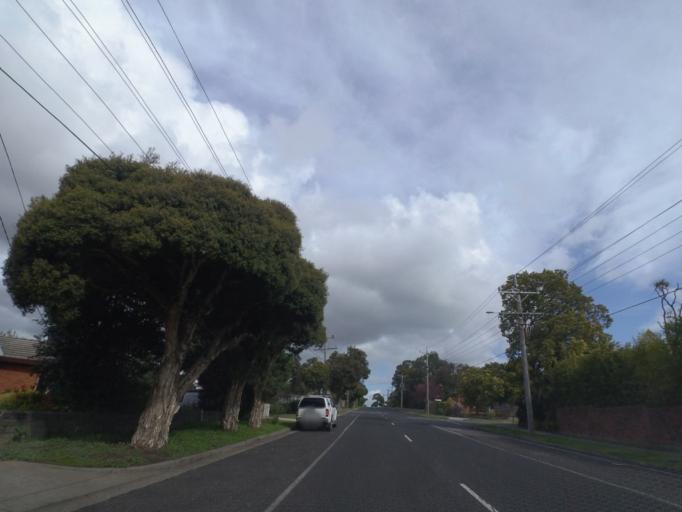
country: AU
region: Victoria
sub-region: Knox
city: Wantirna
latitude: -37.8347
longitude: 145.2134
